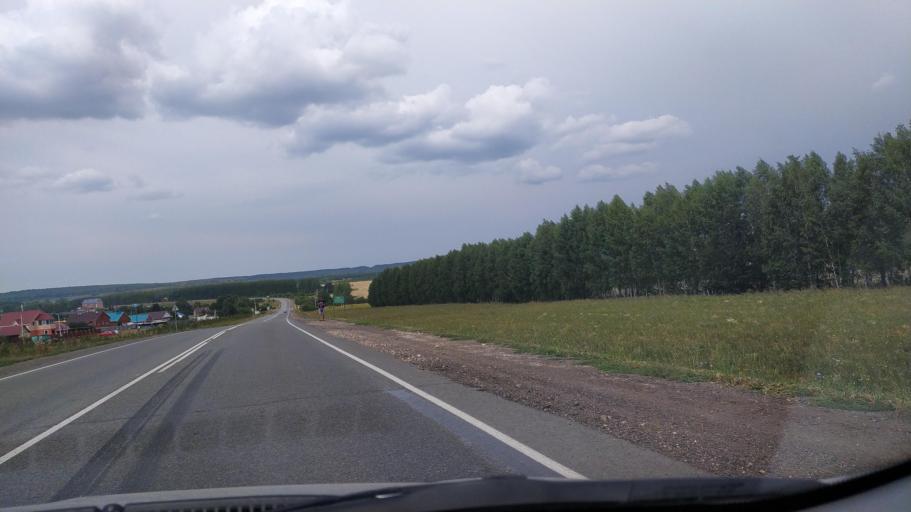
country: RU
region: Tatarstan
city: Al'met'yevsk
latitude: 54.9013
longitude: 52.2108
